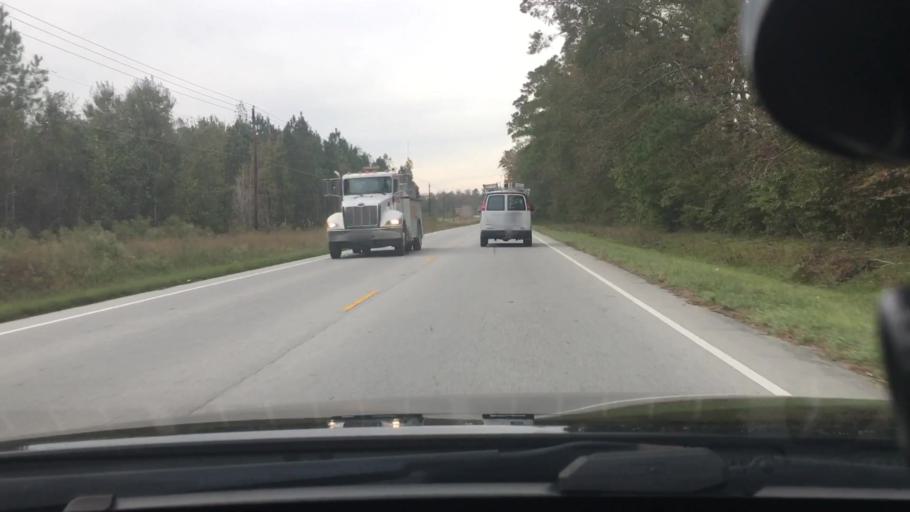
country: US
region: North Carolina
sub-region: Craven County
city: Vanceboro
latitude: 35.2450
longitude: -77.0838
